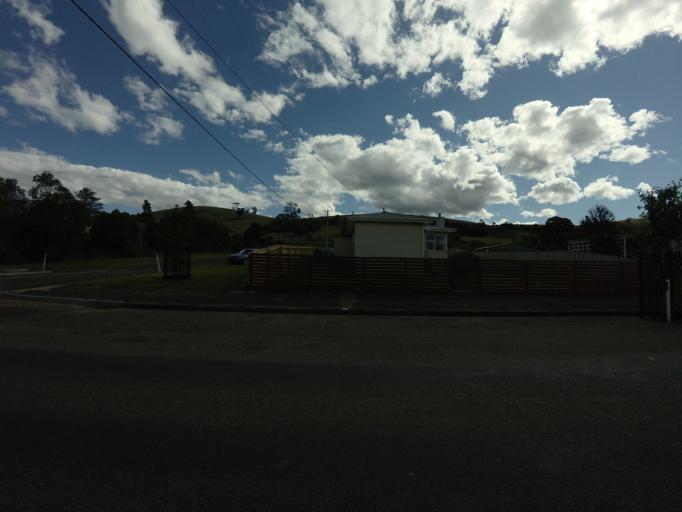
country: AU
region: Tasmania
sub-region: Brighton
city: Bridgewater
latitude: -42.5358
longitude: 147.3654
